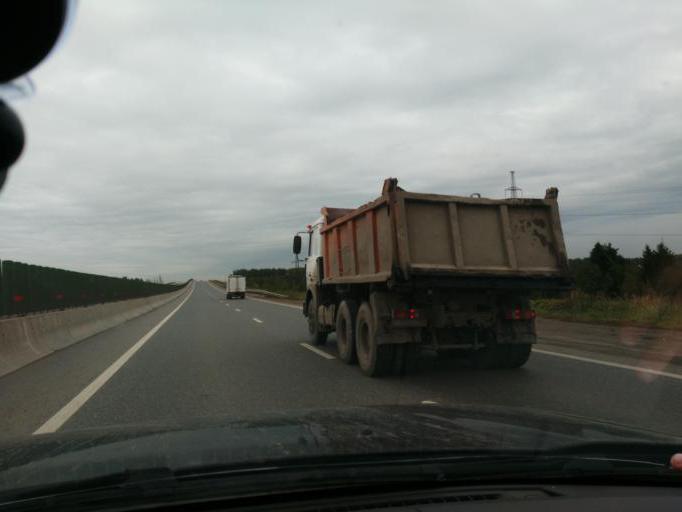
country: RU
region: Perm
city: Froly
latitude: 57.9319
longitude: 56.2838
